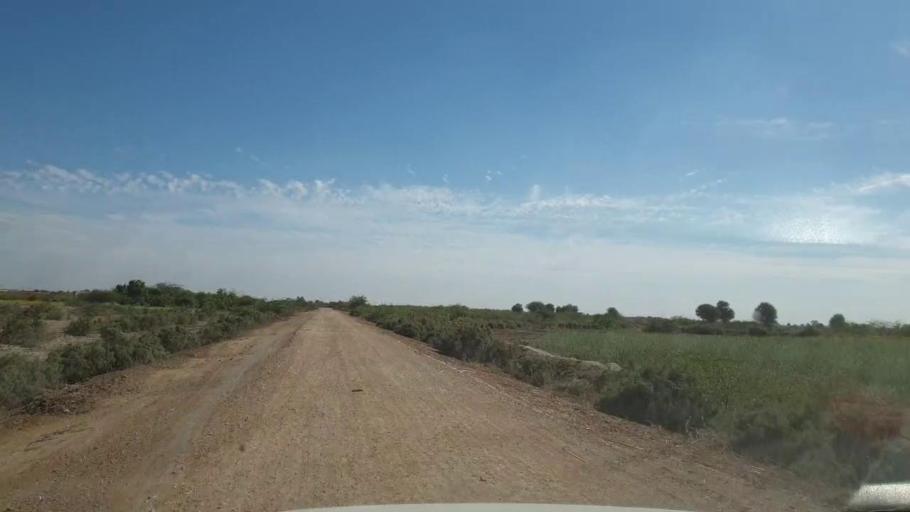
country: PK
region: Sindh
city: Pithoro
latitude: 25.5891
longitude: 69.2856
